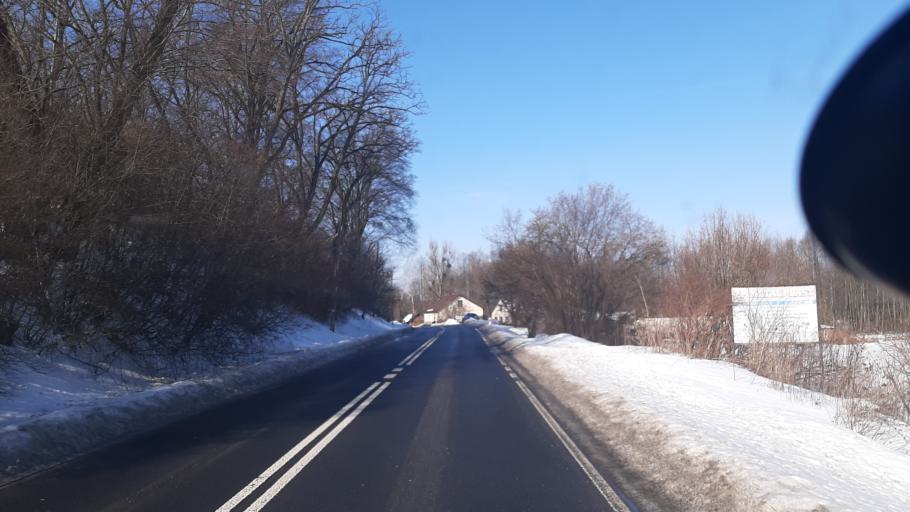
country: PL
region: Lublin Voivodeship
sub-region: Powiat pulawski
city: Wawolnica
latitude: 51.2895
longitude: 22.1613
